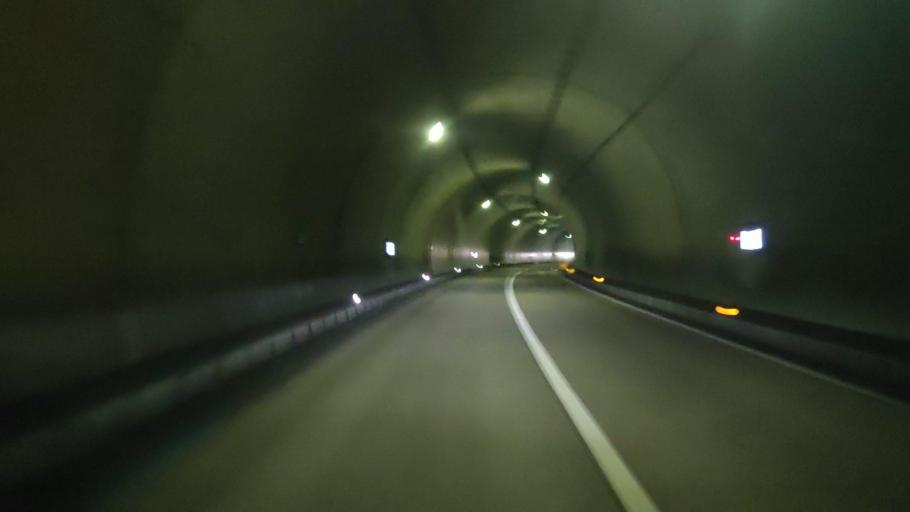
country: JP
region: Wakayama
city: Shingu
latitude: 33.8577
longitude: 135.8520
